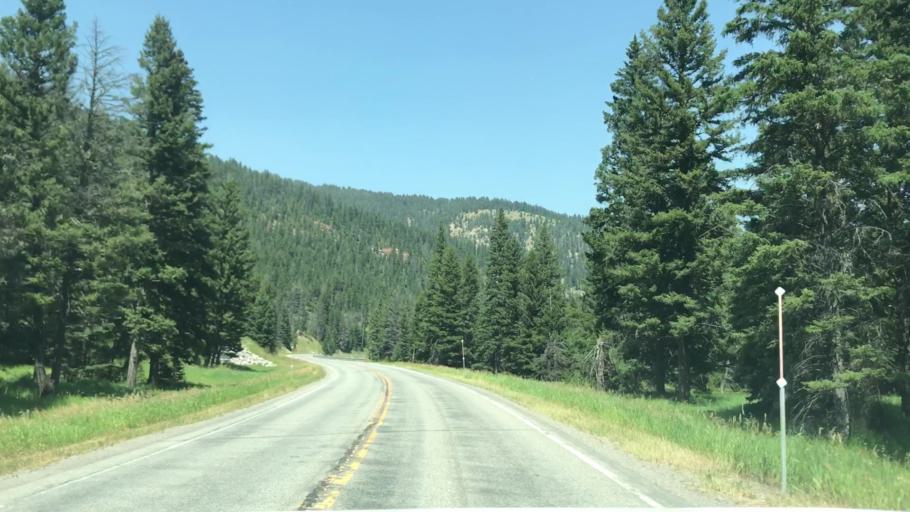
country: US
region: Montana
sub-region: Gallatin County
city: Big Sky
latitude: 45.1567
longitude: -111.2463
